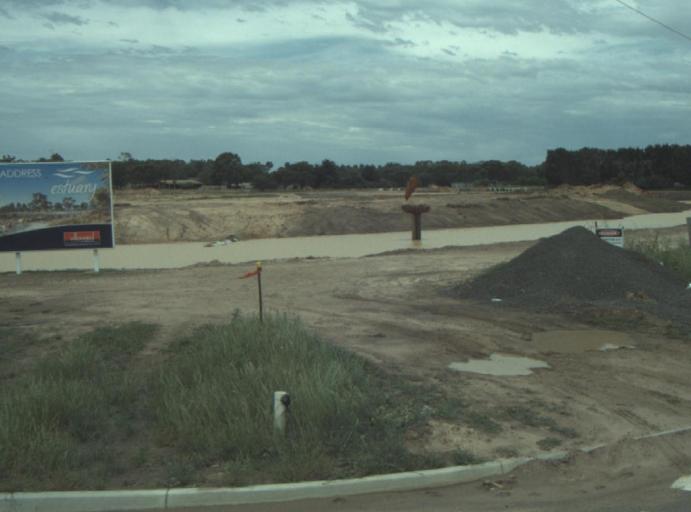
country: AU
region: Victoria
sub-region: Greater Geelong
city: Leopold
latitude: -38.2010
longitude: 144.4527
